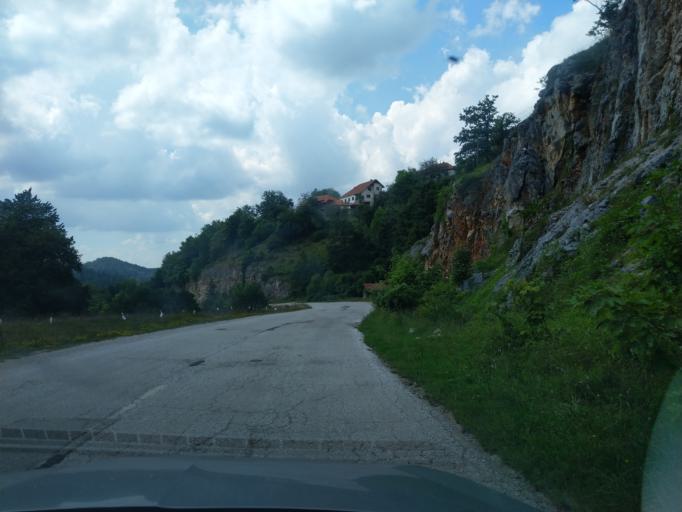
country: RS
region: Central Serbia
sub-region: Zlatiborski Okrug
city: Nova Varos
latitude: 43.5395
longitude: 19.9085
